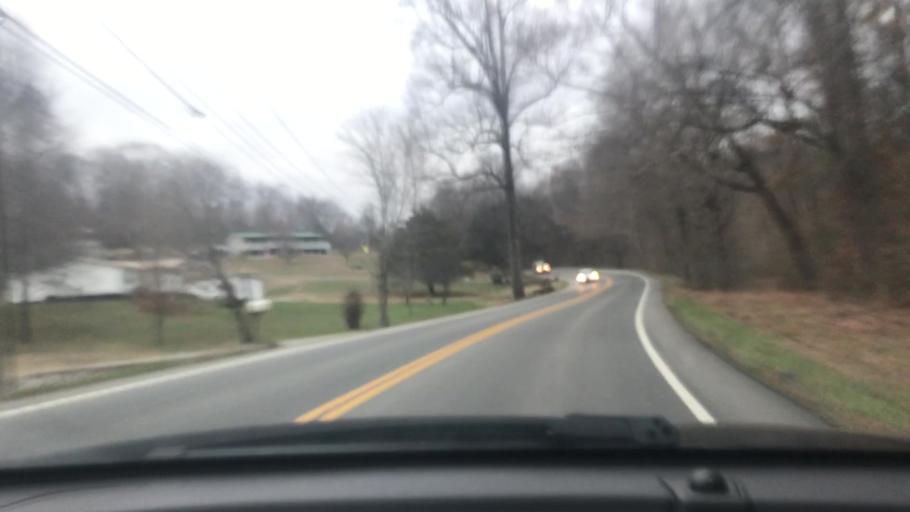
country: US
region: Tennessee
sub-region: Dickson County
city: Charlotte
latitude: 36.2443
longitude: -87.3479
